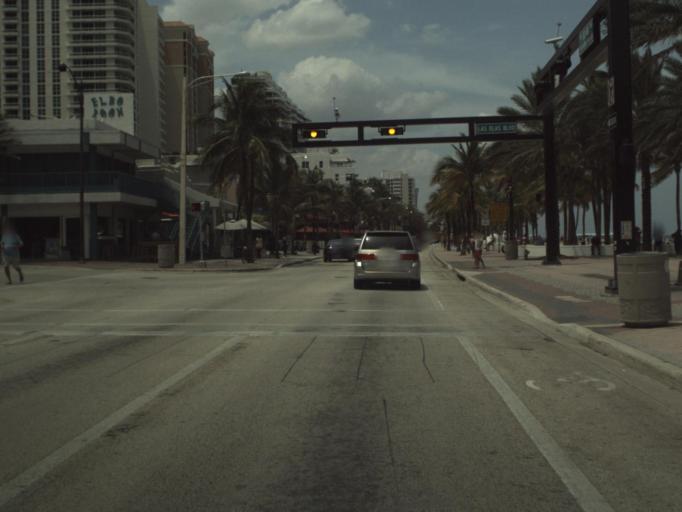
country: US
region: Florida
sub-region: Broward County
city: Sunrise
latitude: 26.1190
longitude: -80.1046
